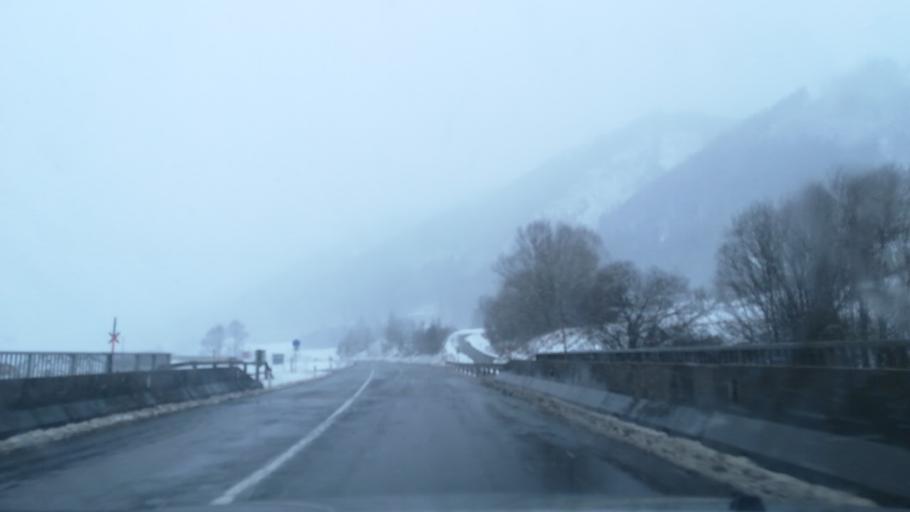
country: AT
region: Styria
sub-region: Politischer Bezirk Murtal
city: Sankt Peter ob Judenburg
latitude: 47.1909
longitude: 14.5999
